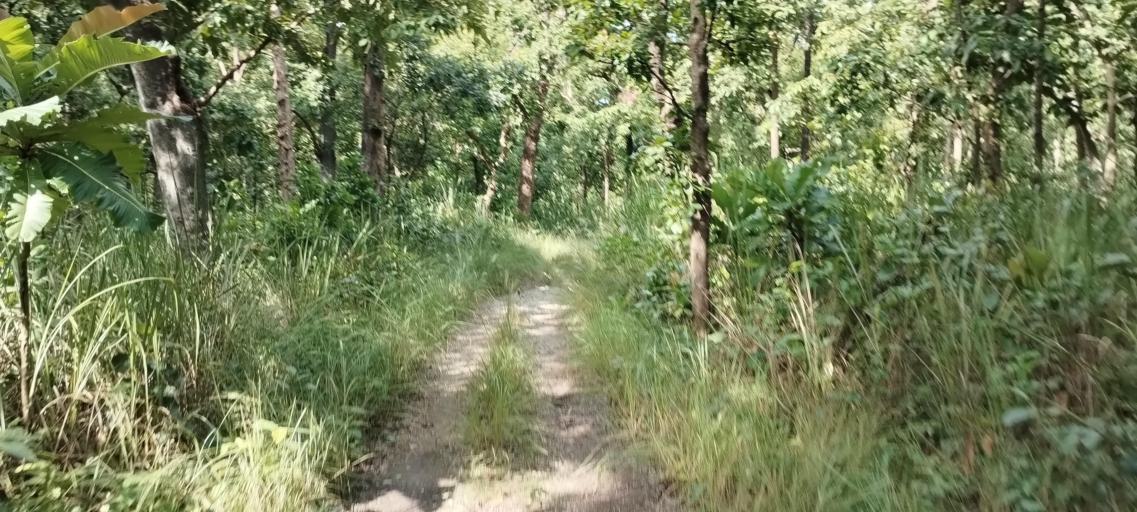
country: NP
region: Far Western
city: Tikapur
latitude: 28.5563
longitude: 81.2924
